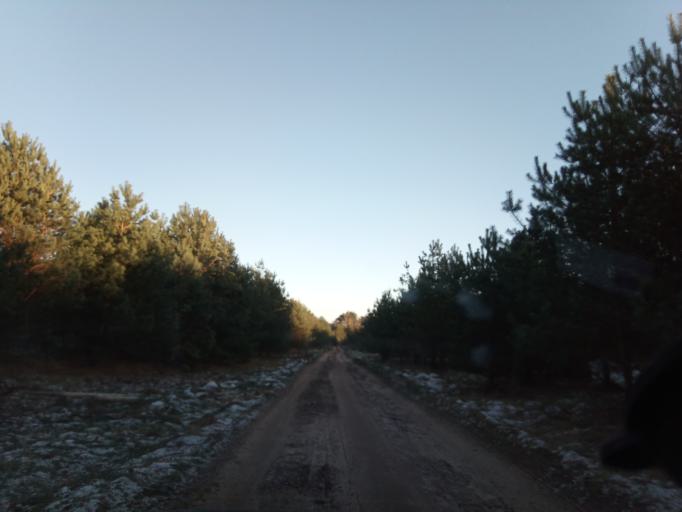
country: LT
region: Alytaus apskritis
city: Druskininkai
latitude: 53.9728
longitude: 23.9568
